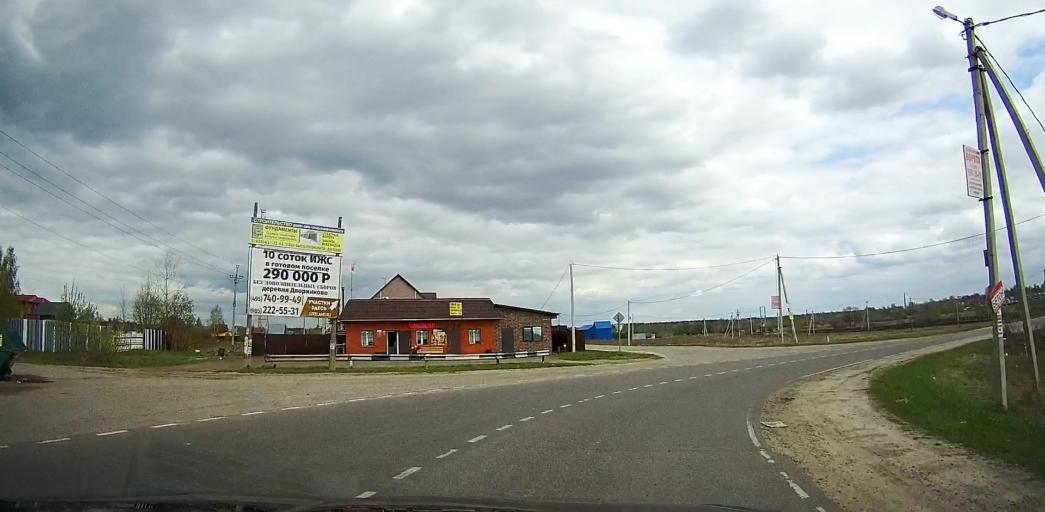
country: RU
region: Moskovskaya
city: Imeni Tsyurupy
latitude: 55.4976
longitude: 38.6230
